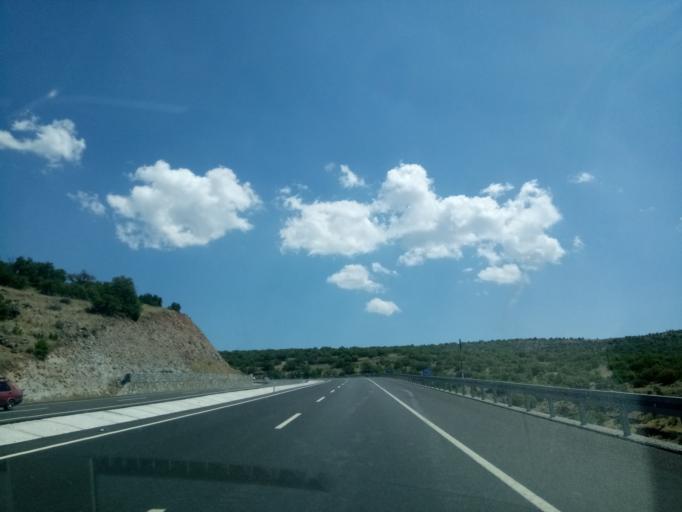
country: TR
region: Konya
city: Cavus
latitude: 37.6529
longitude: 31.9592
